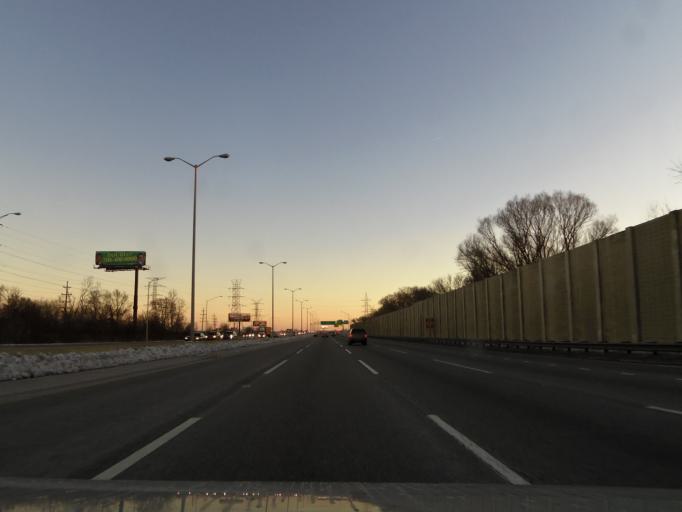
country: US
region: Illinois
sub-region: Cook County
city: Hickory Hills
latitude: 41.7250
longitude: -87.8096
